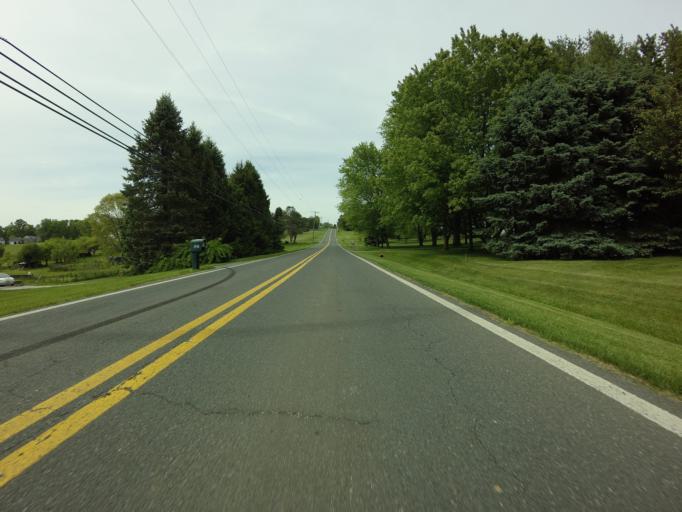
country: US
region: Maryland
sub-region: Carroll County
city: Eldersburg
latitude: 39.4636
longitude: -76.9538
